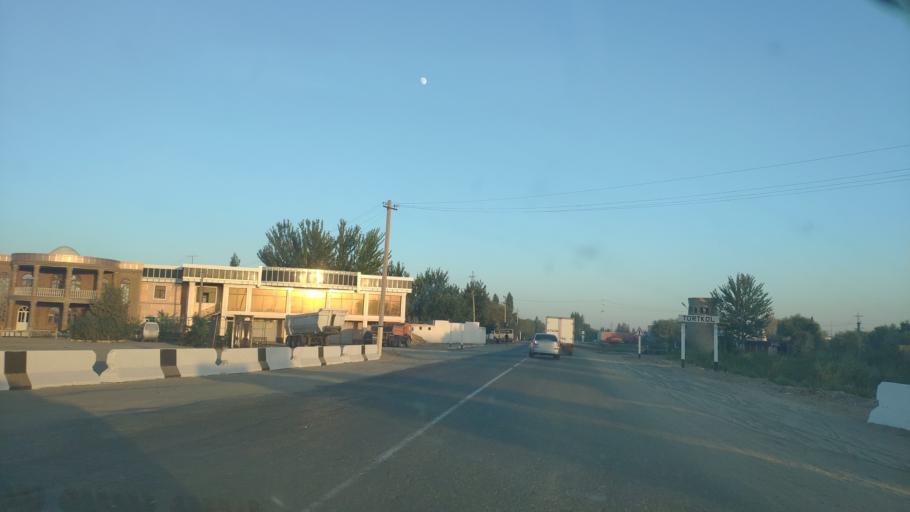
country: UZ
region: Karakalpakstan
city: To'rtko'l Shahri
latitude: 41.5679
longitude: 60.9515
